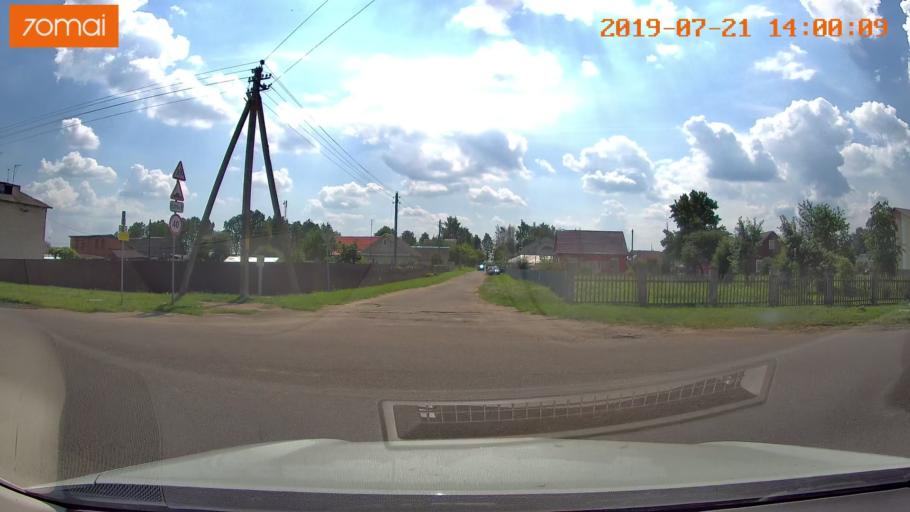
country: BY
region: Grodnenskaya
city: Lyubcha
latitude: 53.7507
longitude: 26.0626
